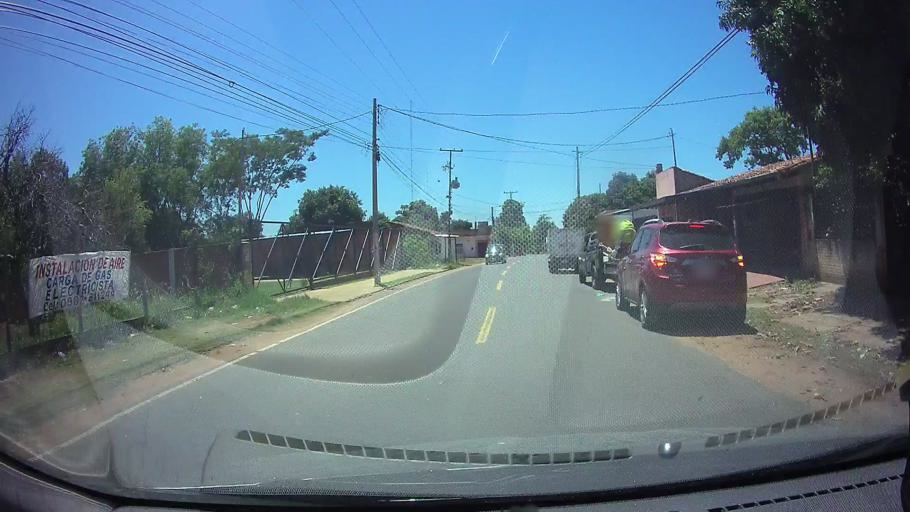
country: PY
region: Central
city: San Lorenzo
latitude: -25.3178
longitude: -57.4934
